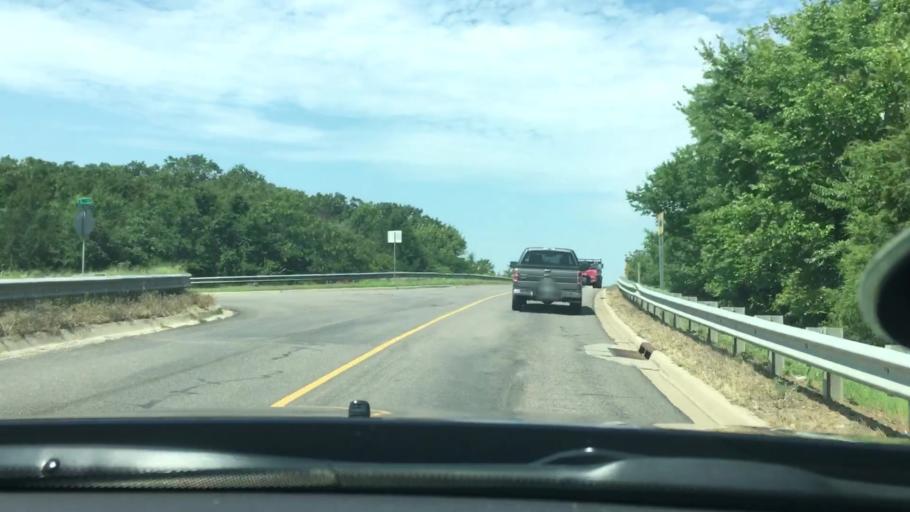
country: US
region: Oklahoma
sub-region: Pontotoc County
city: Ada
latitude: 34.7908
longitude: -96.6422
